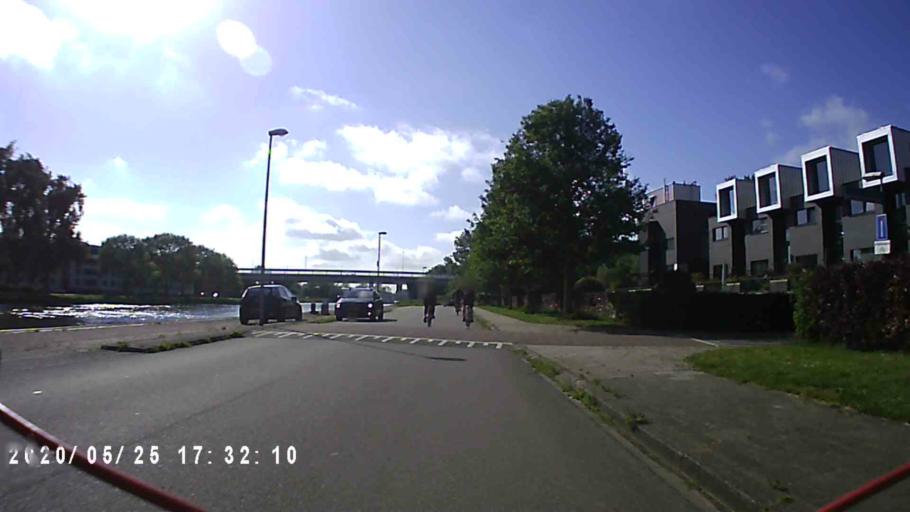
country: NL
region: Groningen
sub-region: Gemeente Groningen
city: Korrewegwijk
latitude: 53.2387
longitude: 6.5714
